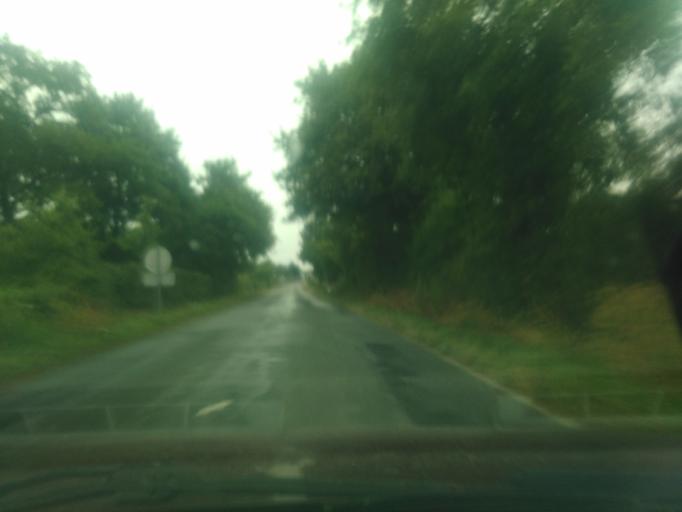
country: FR
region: Pays de la Loire
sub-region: Departement de la Vendee
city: La Ferriere
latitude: 46.7635
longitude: -1.3050
